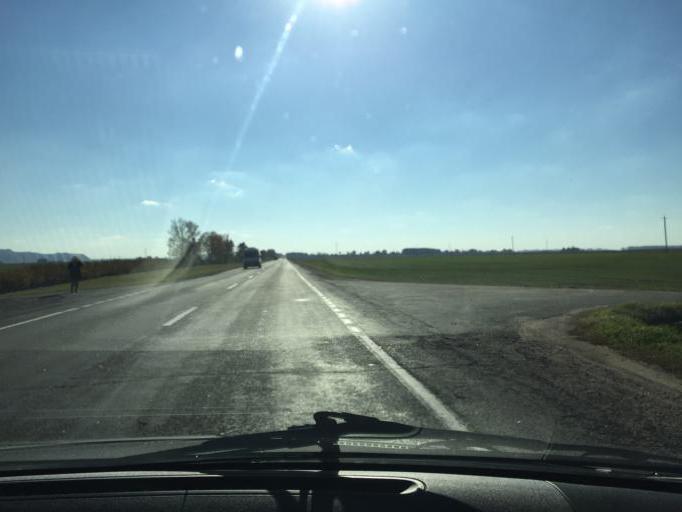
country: BY
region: Minsk
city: Slutsk
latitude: 52.9327
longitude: 27.4877
